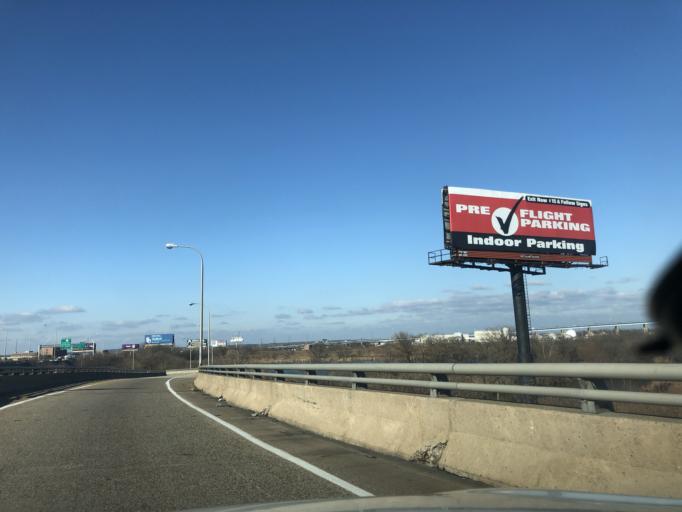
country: US
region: New Jersey
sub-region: Gloucester County
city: National Park
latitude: 39.8863
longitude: -75.2117
